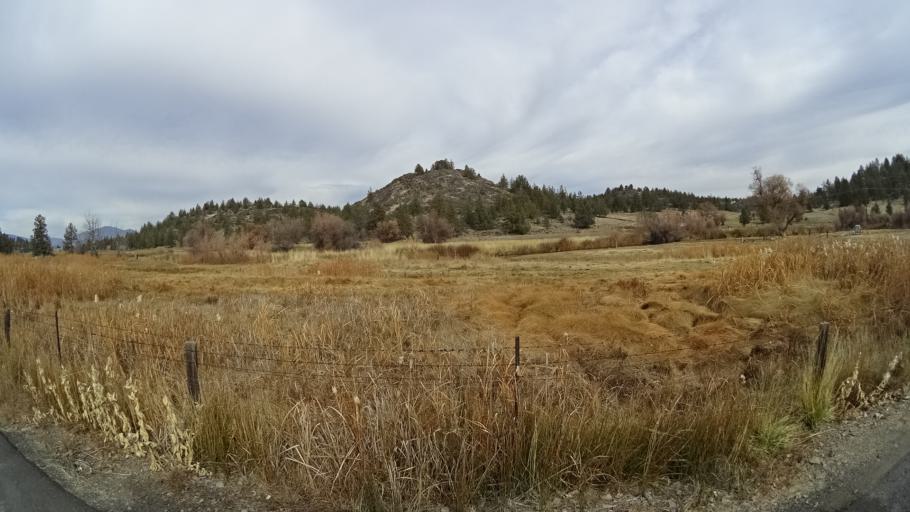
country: US
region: California
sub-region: Siskiyou County
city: Montague
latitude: 41.6824
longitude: -122.5167
